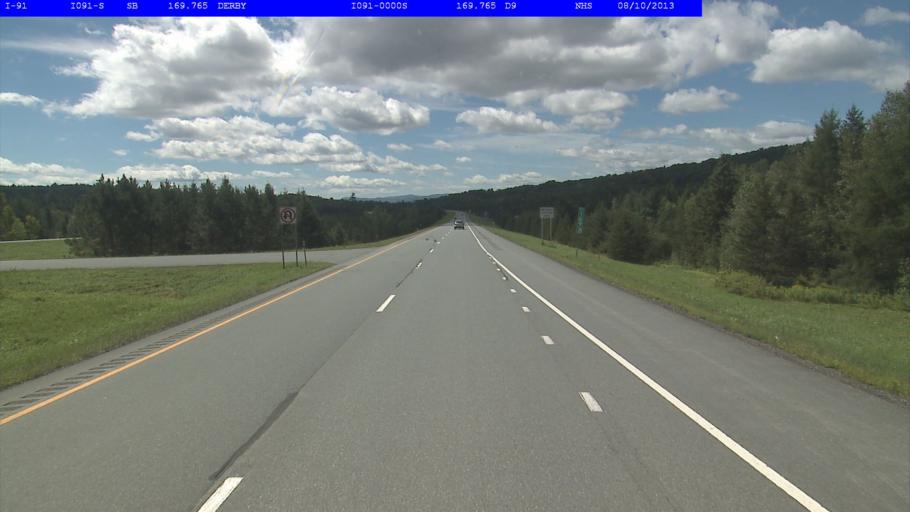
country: US
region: Vermont
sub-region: Orleans County
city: Newport
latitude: 44.9188
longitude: -72.1754
